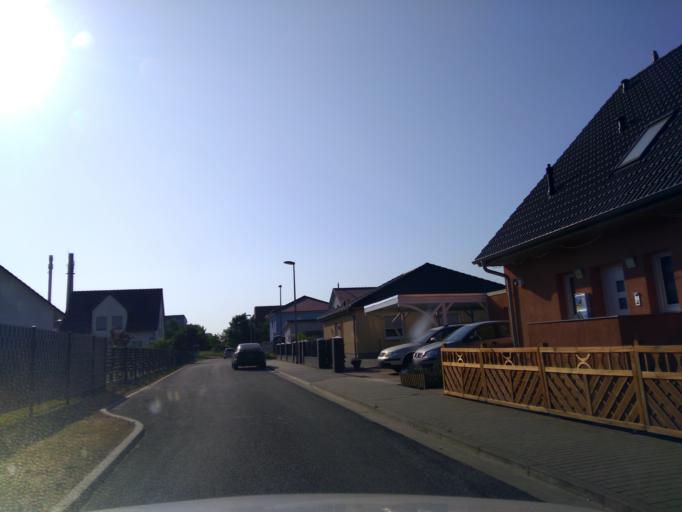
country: DE
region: Brandenburg
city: Dallgow-Doeberitz
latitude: 52.5631
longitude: 13.0669
